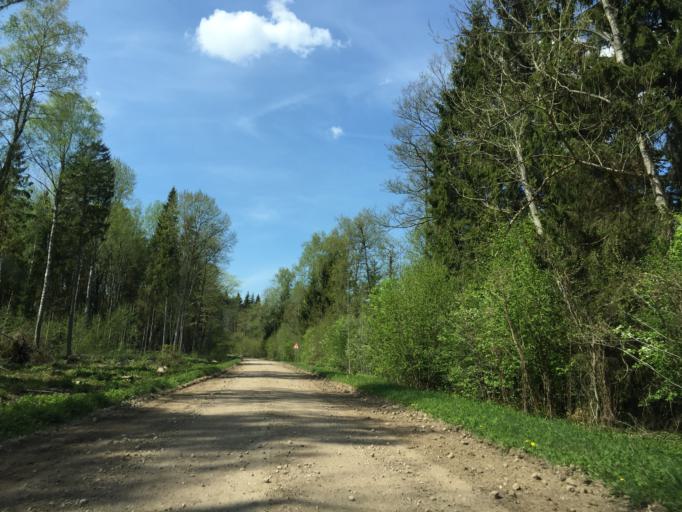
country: LV
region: Limbazu Rajons
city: Limbazi
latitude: 57.3878
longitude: 24.5993
